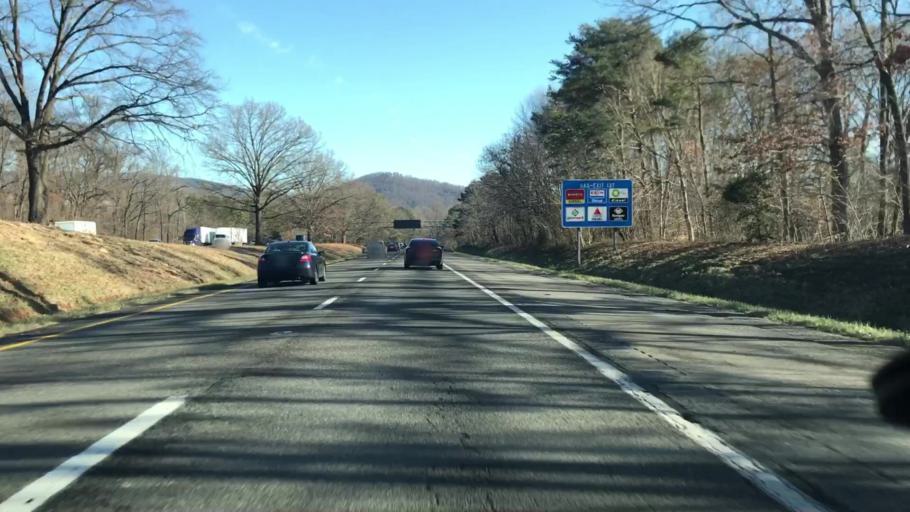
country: US
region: Virginia
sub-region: City of Salem
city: Salem
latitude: 37.2851
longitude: -80.1238
